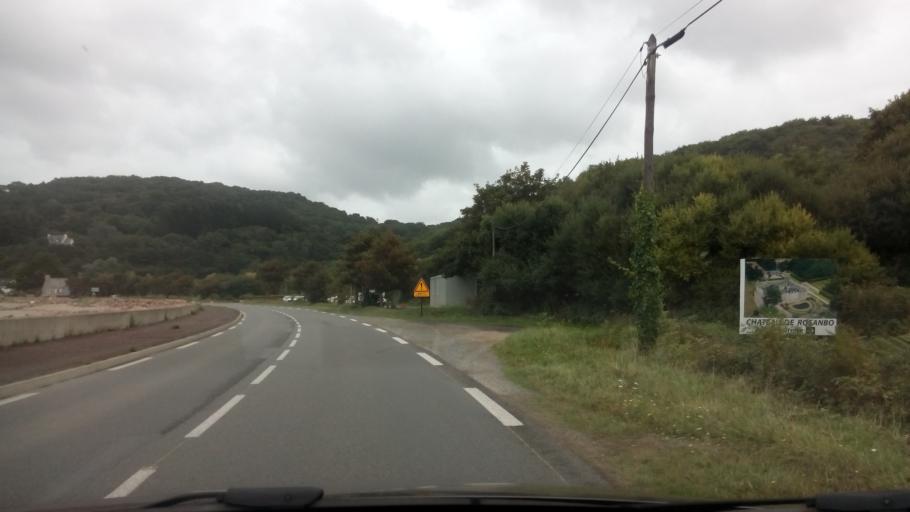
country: FR
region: Brittany
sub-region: Departement des Cotes-d'Armor
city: Plestin-les-Greves
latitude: 48.6702
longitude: -3.5832
